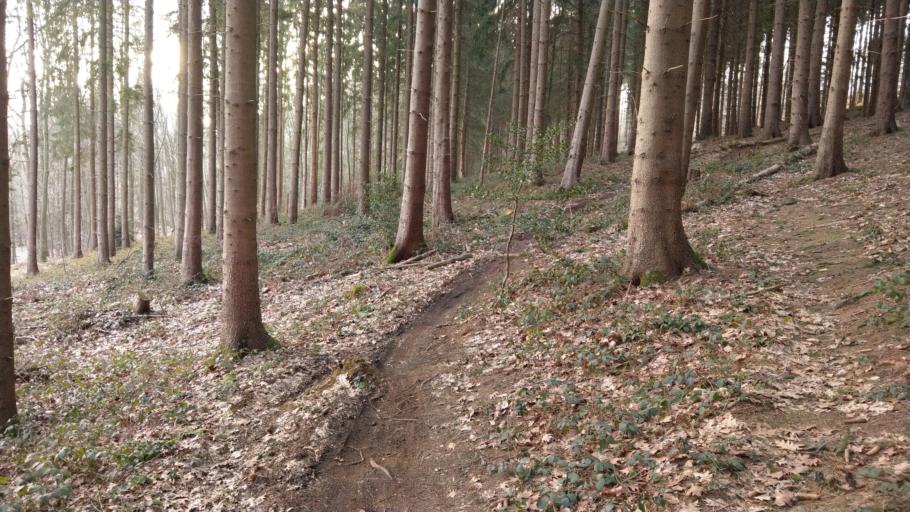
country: NL
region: Limburg
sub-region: Gemeente Vaals
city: Vaals
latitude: 50.7450
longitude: 6.0462
